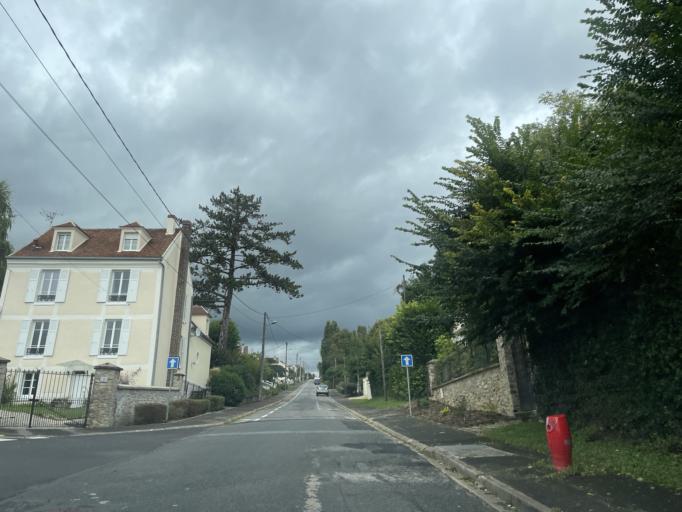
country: FR
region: Ile-de-France
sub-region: Departement de Seine-et-Marne
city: Coulommiers
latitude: 48.8220
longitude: 3.0861
